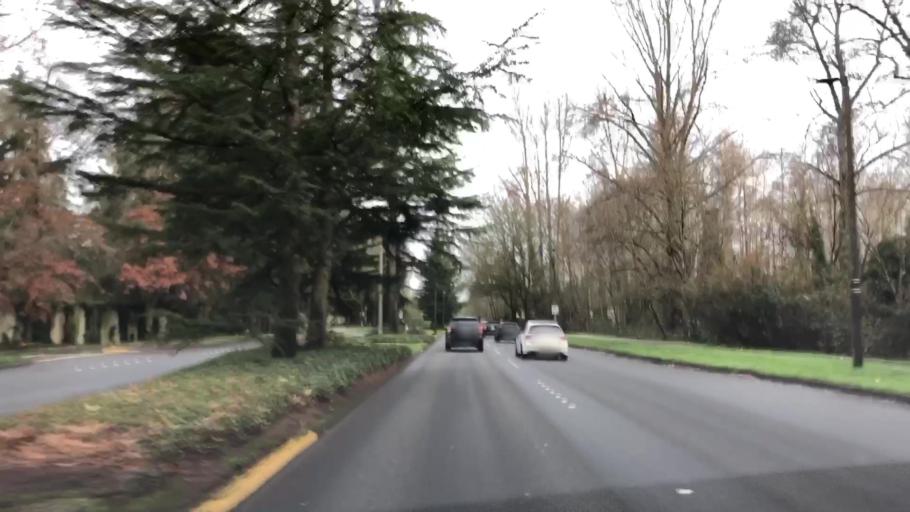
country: US
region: Washington
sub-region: King County
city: Eastgate
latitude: 47.6126
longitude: -122.1430
